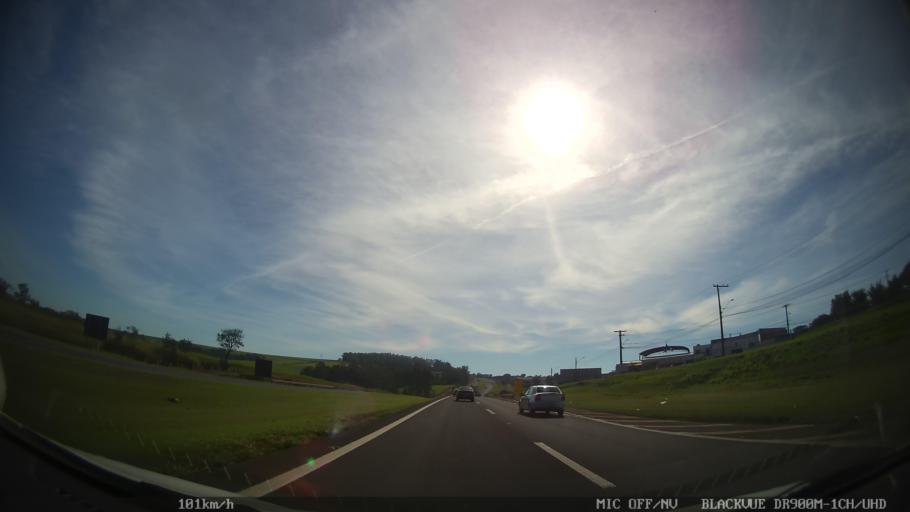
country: BR
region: Sao Paulo
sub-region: Araras
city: Araras
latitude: -22.3445
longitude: -47.3933
